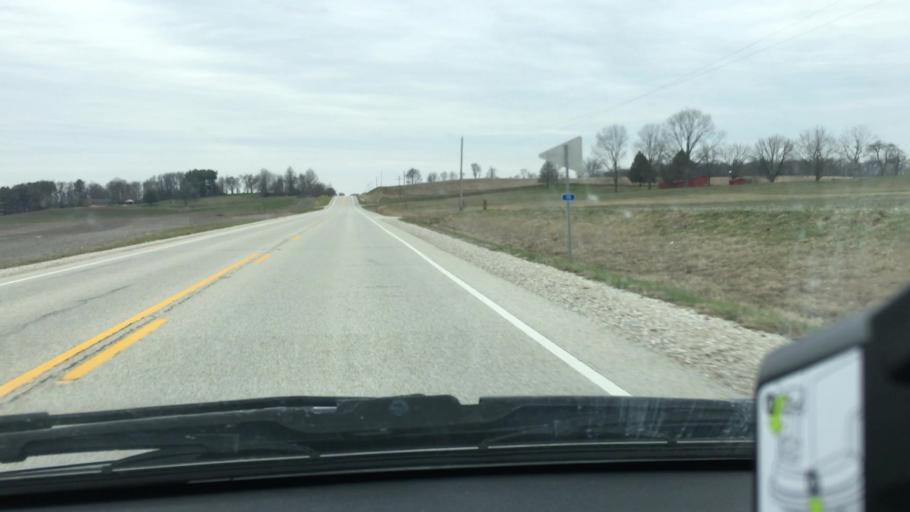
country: US
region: Indiana
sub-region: Greene County
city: Bloomfield
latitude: 38.9575
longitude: -87.0167
